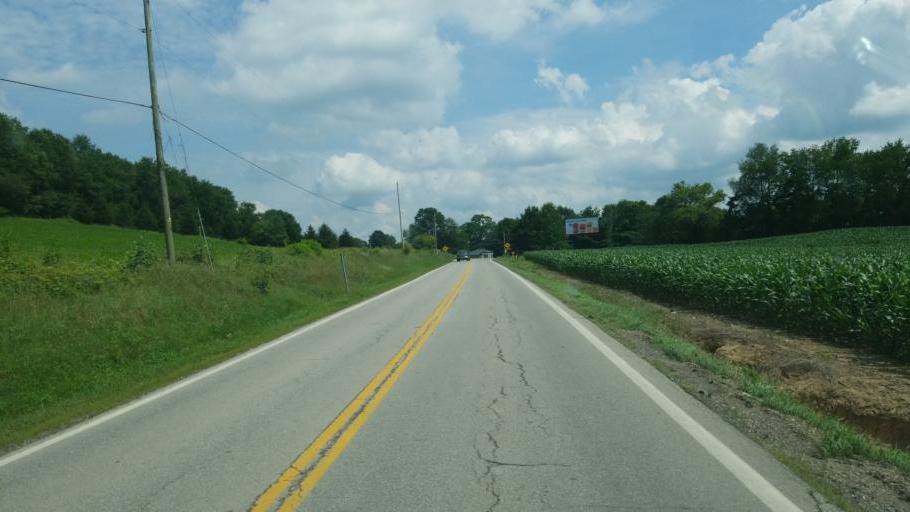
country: US
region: Ohio
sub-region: Richland County
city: Lexington
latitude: 40.6695
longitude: -82.5624
